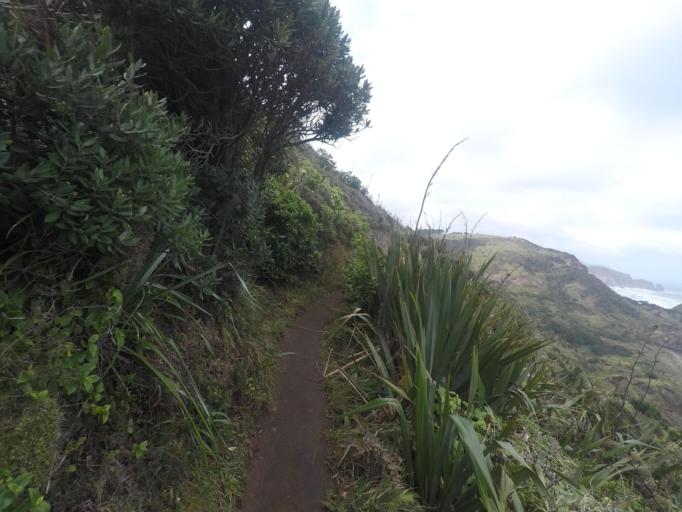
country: NZ
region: Auckland
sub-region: Auckland
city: Muriwai Beach
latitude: -36.8792
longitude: 174.4380
